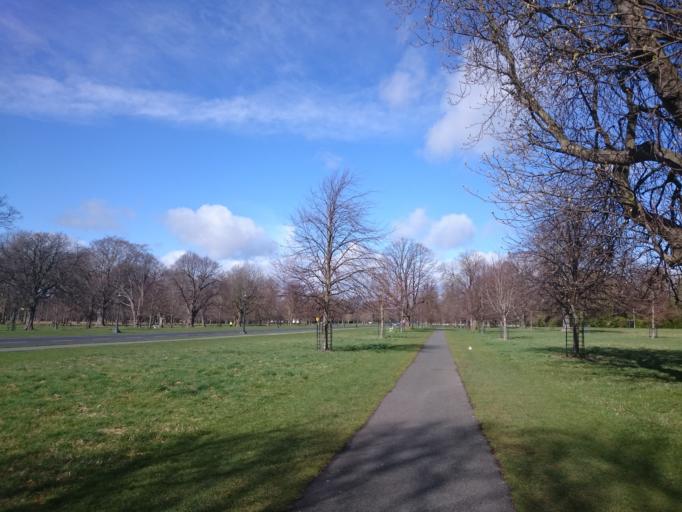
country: IE
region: Leinster
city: Chapelizod
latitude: 53.3583
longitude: -6.3207
